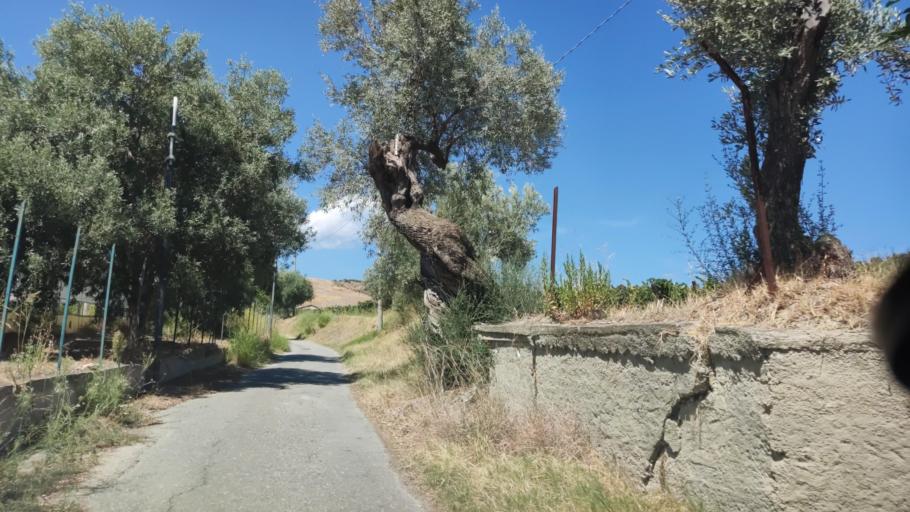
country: IT
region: Calabria
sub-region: Provincia di Reggio Calabria
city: Monasterace
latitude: 38.4397
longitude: 16.5546
